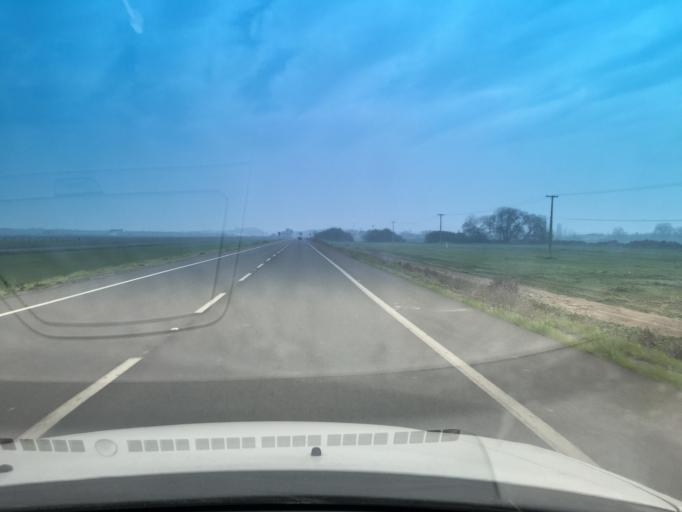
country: CL
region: Santiago Metropolitan
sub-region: Provincia de Santiago
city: Lo Prado
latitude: -33.3716
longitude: -70.7991
